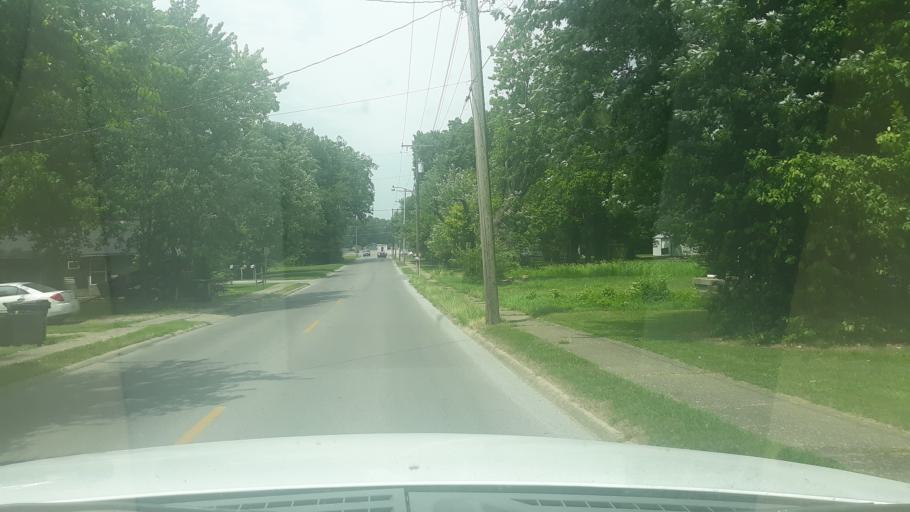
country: US
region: Illinois
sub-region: Saline County
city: Harrisburg
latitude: 37.7257
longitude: -88.5530
